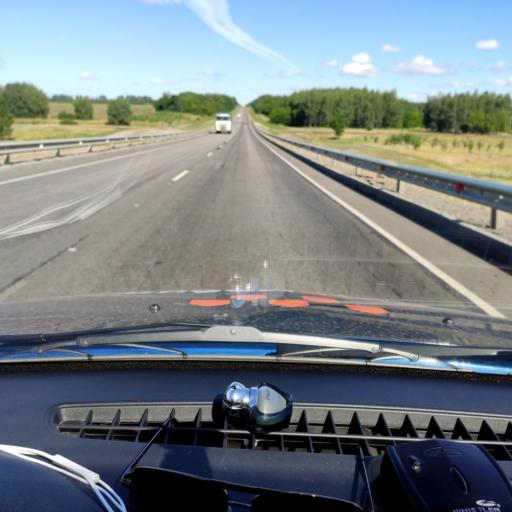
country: RU
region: Lipetsk
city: Khlevnoye
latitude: 52.1617
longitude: 39.1390
